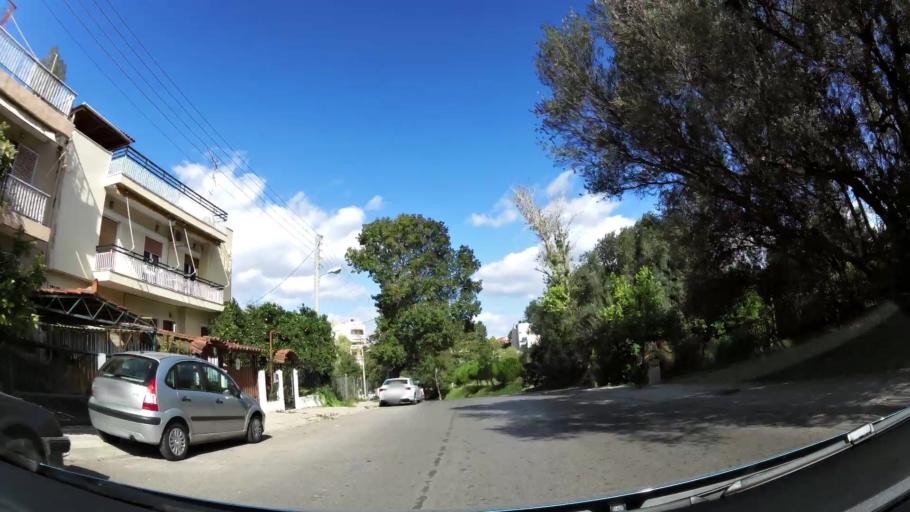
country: GR
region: Attica
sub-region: Nomarchia Athinas
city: Khalandrion
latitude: 38.0128
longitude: 23.8024
